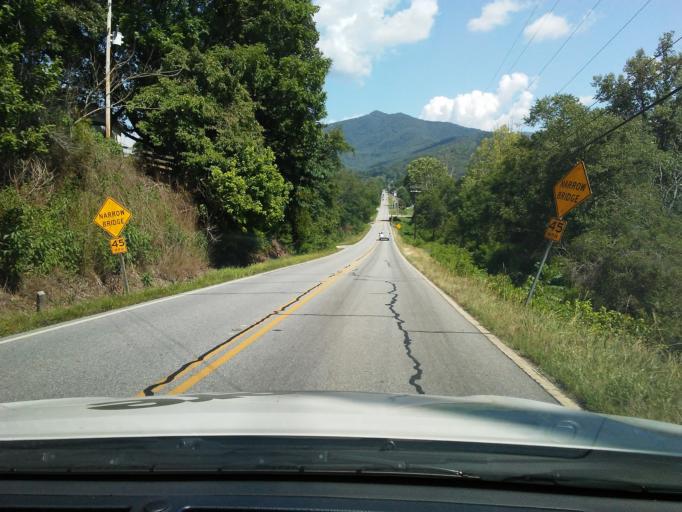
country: US
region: Georgia
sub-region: Towns County
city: Hiawassee
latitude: 34.9413
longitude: -83.8586
